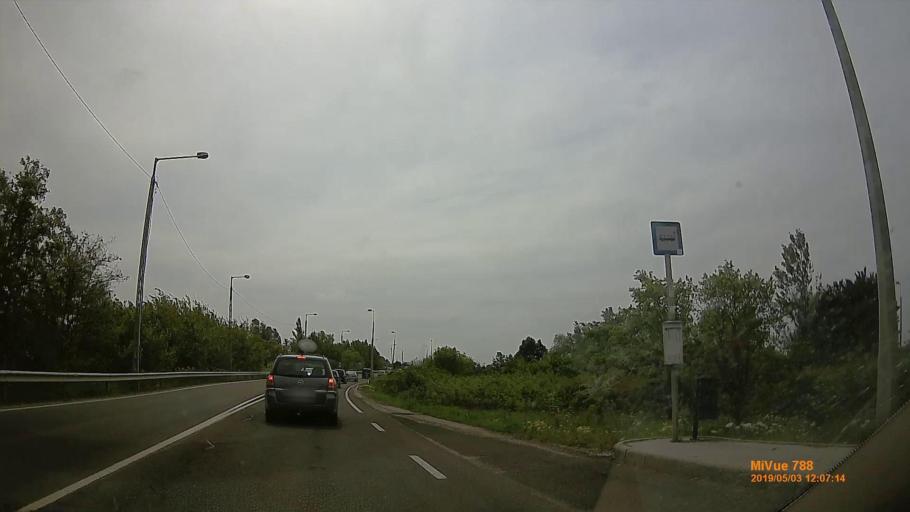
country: HU
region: Jasz-Nagykun-Szolnok
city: Szolnok
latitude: 47.1562
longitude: 20.2034
